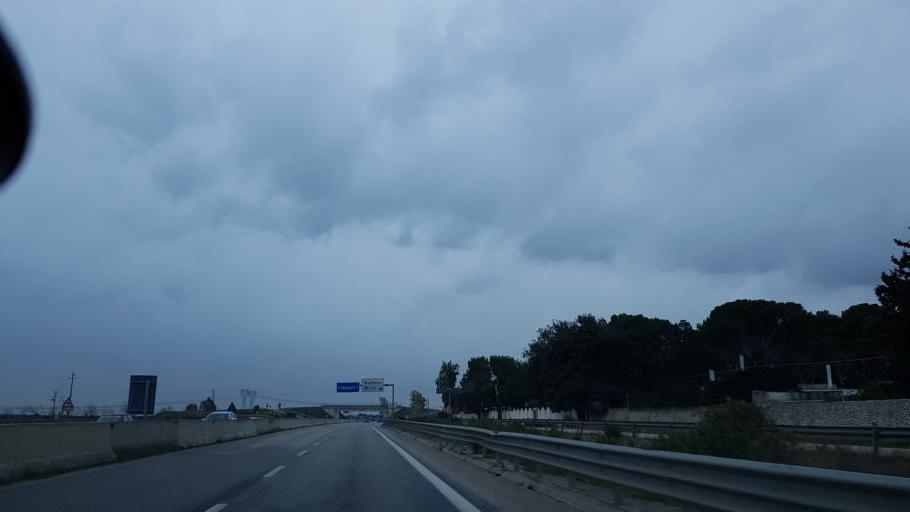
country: IT
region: Apulia
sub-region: Provincia di Brindisi
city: Brindisi
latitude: 40.6067
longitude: 17.8866
